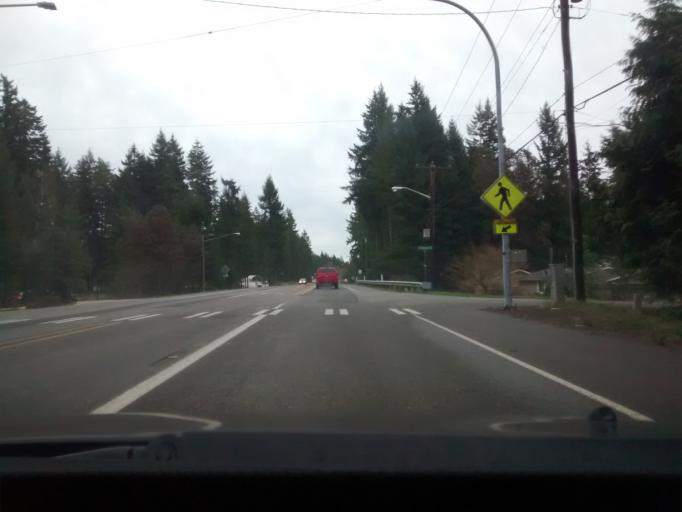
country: US
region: Washington
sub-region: Kitsap County
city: East Port Orchard
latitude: 47.5195
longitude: -122.6183
